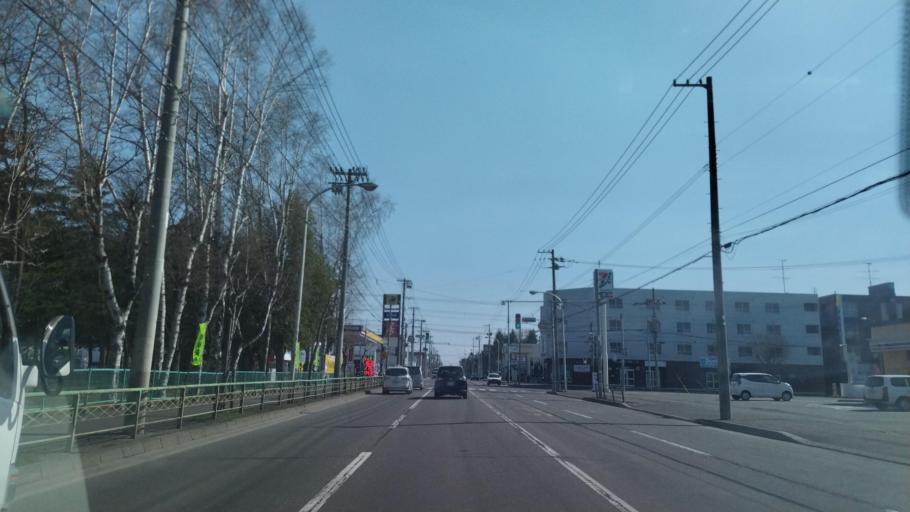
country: JP
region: Hokkaido
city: Obihiro
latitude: 42.9054
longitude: 143.1996
